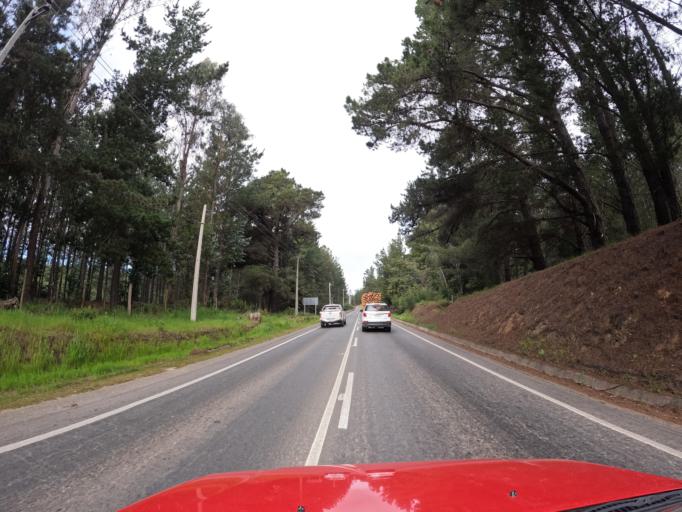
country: CL
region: O'Higgins
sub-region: Provincia de Colchagua
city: Santa Cruz
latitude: -34.3587
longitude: -71.8932
